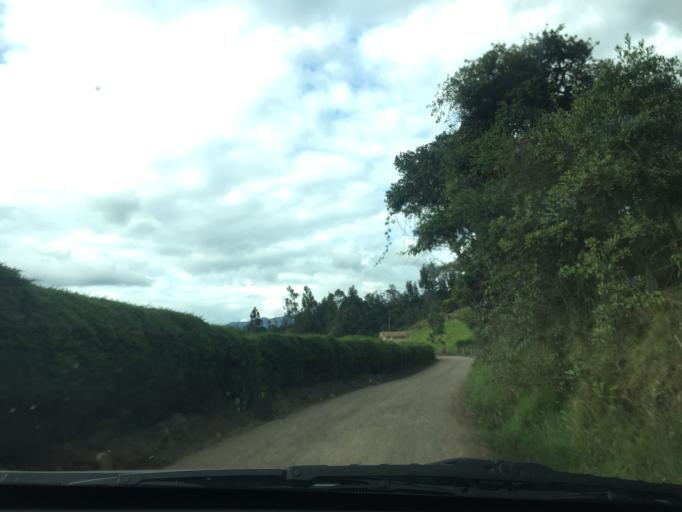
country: CO
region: Cundinamarca
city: Subachoque
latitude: 4.9413
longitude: -74.1446
